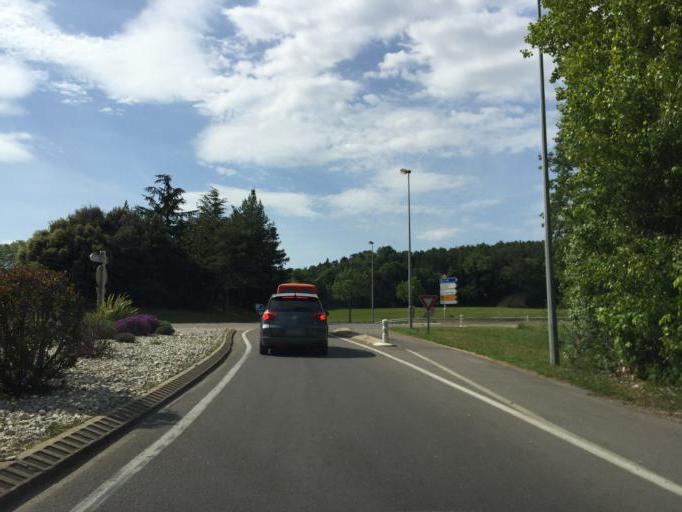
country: FR
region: Rhone-Alpes
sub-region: Departement de la Drome
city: Crest
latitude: 44.7386
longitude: 5.0049
